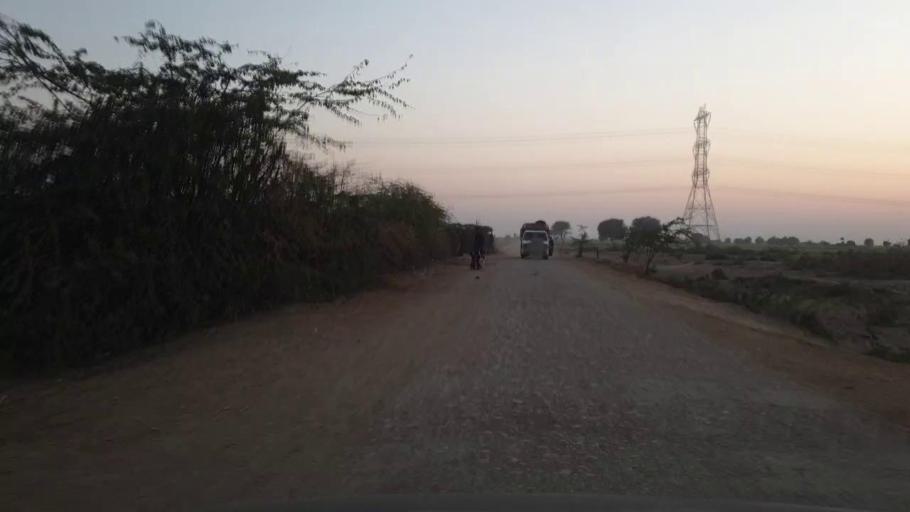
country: PK
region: Sindh
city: Digri
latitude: 25.1972
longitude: 69.1926
